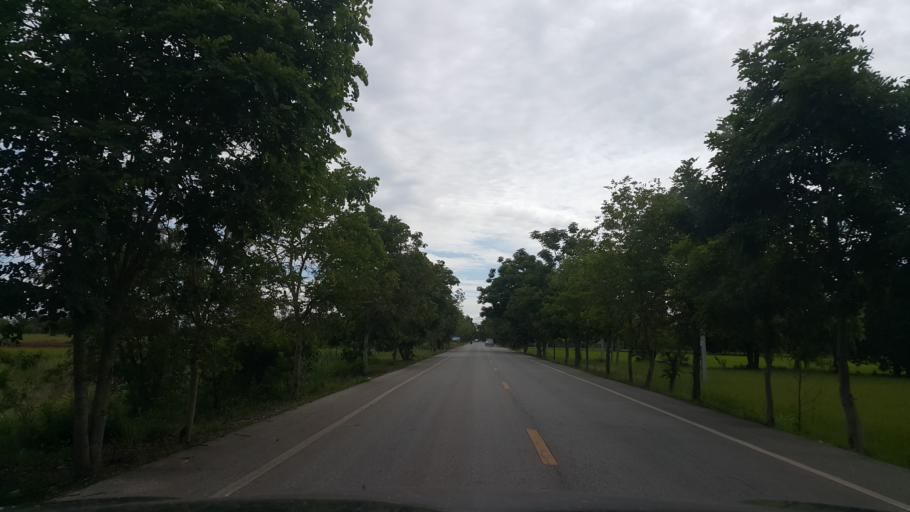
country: TH
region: Uttaradit
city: Phichai
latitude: 17.2992
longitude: 100.1036
